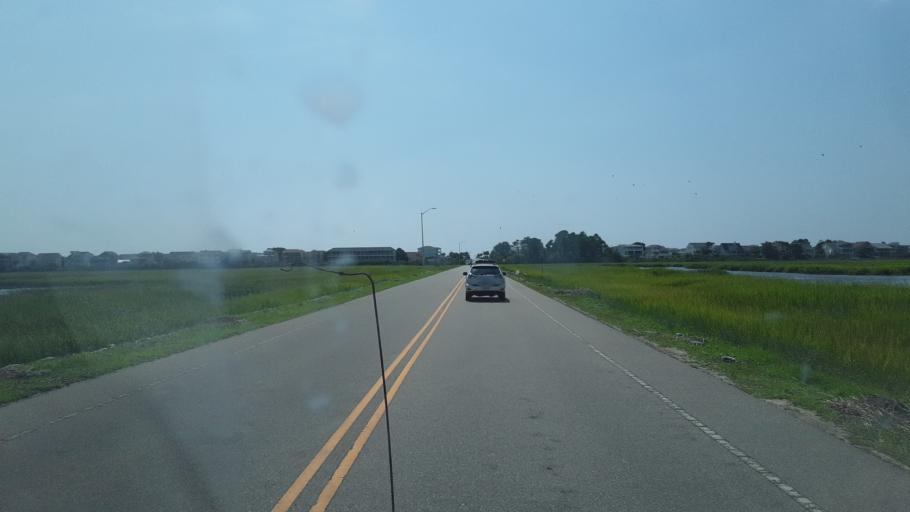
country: US
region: North Carolina
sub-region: Brunswick County
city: Sunset Beach
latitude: 33.8760
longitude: -78.5093
